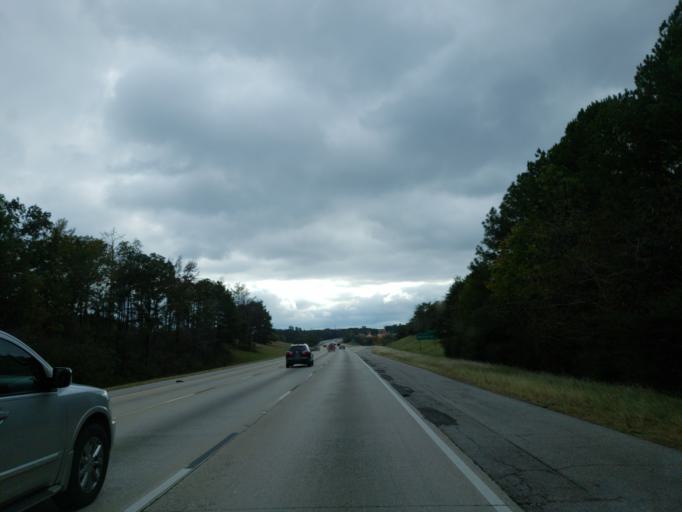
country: US
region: Alabama
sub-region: Jefferson County
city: Vestavia Hills
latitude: 33.4166
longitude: -86.7556
